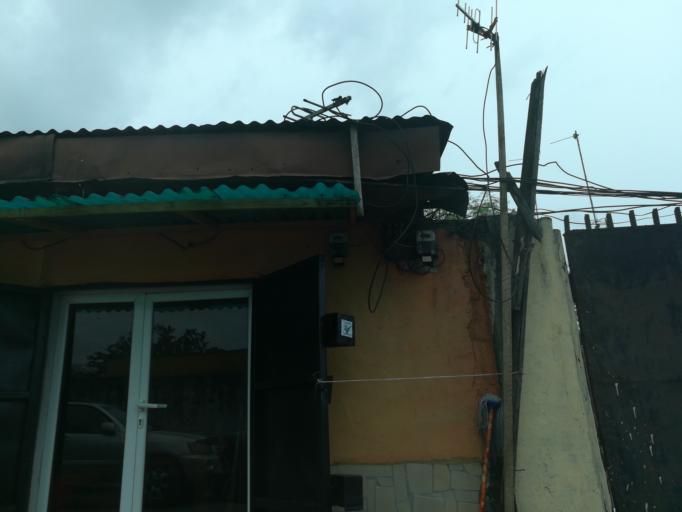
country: NG
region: Rivers
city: Port Harcourt
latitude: 4.8257
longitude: 7.0271
